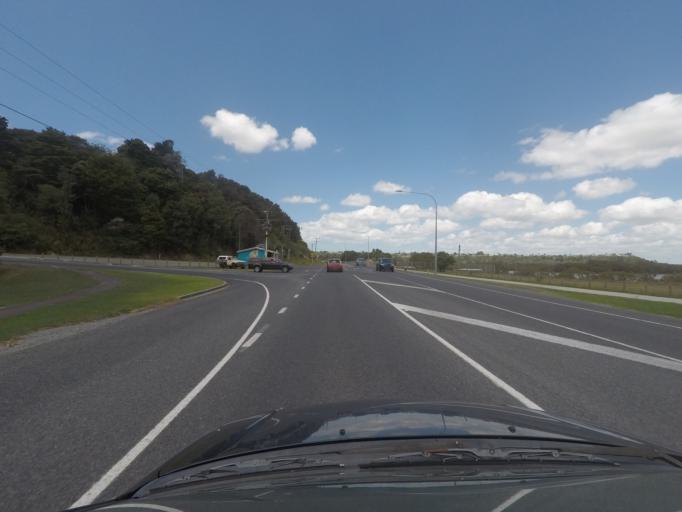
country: NZ
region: Northland
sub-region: Whangarei
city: Whangarei
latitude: -35.7355
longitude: 174.3512
